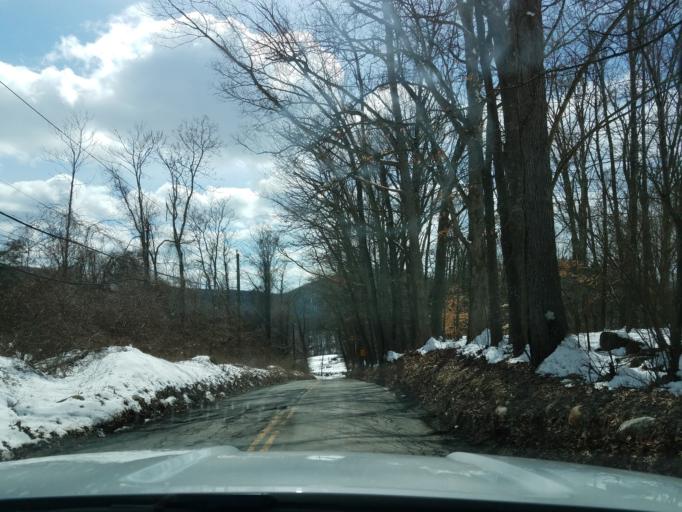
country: US
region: Connecticut
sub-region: Litchfield County
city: New Milford
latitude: 41.5548
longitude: -73.3930
